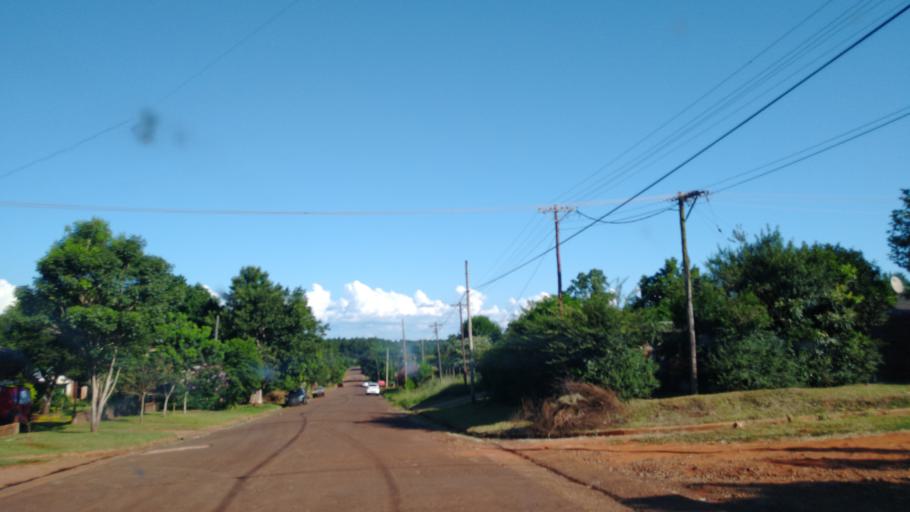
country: AR
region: Misiones
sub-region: Departamento de San Ignacio
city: San Ignacio
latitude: -27.2616
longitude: -55.5400
